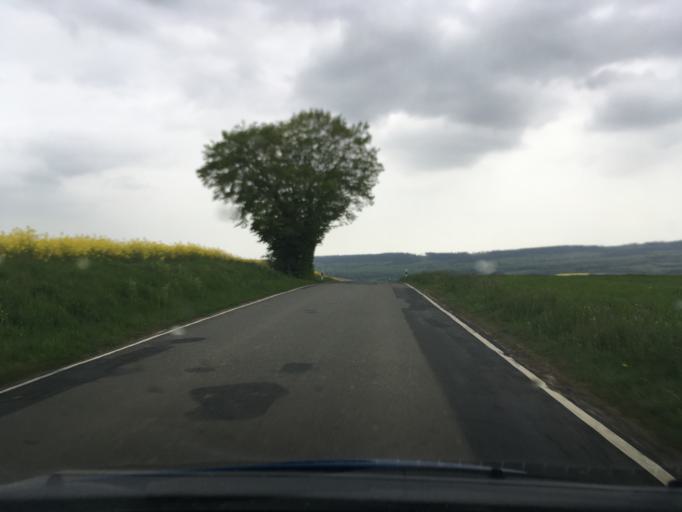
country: DE
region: Lower Saxony
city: Eimen
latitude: 51.8554
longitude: 9.8105
